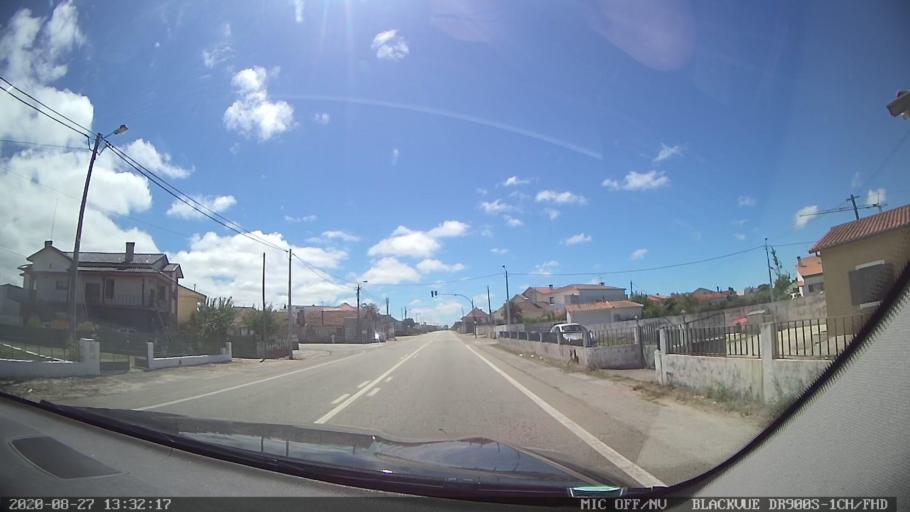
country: PT
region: Aveiro
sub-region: Vagos
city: Vagos
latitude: 40.4891
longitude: -8.6869
